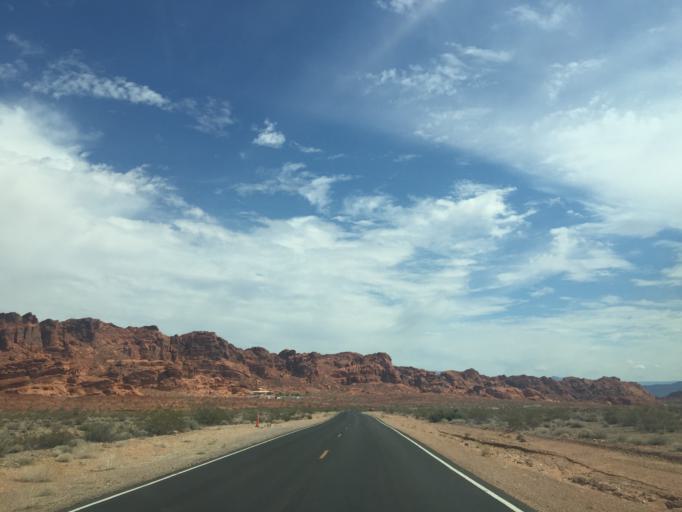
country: US
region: Nevada
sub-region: Clark County
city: Moapa Valley
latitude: 36.4249
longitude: -114.5220
